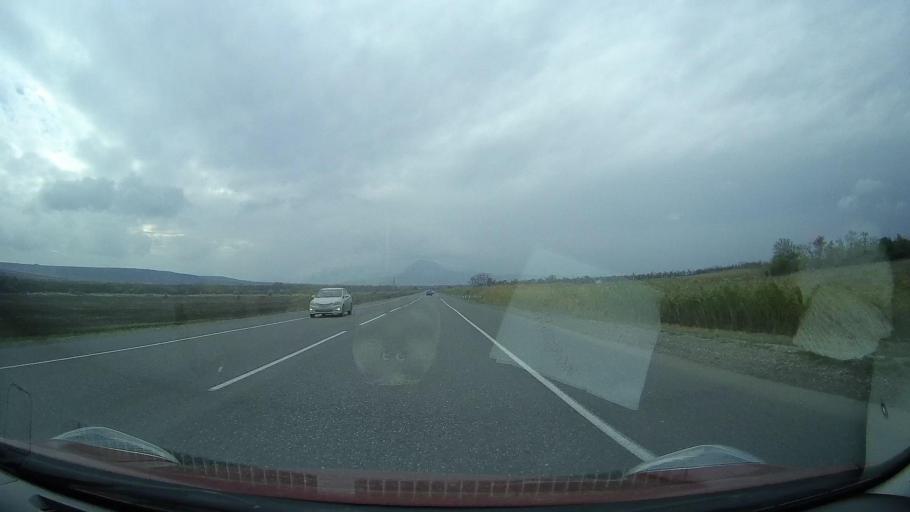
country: RU
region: Stavropol'skiy
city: Levokumka
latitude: 44.2346
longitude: 43.2263
